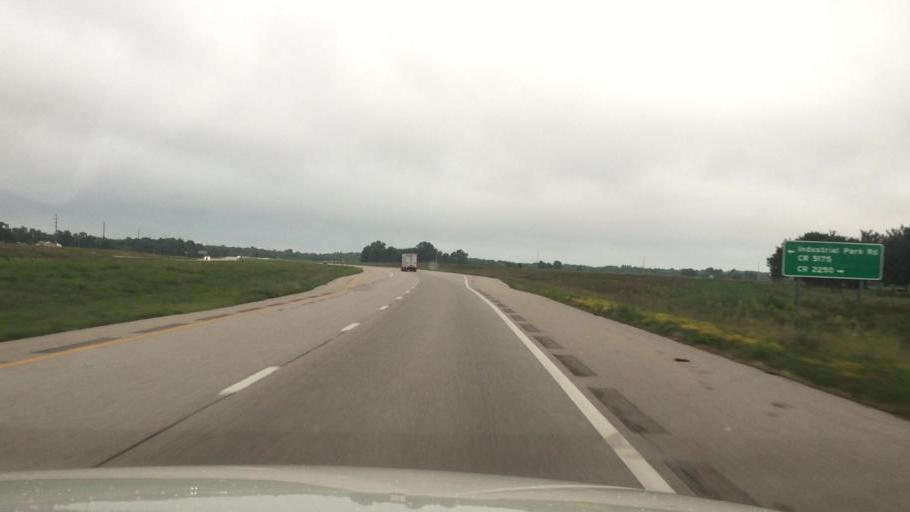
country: US
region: Kansas
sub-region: Montgomery County
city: Coffeyville
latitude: 37.0768
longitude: -95.5895
